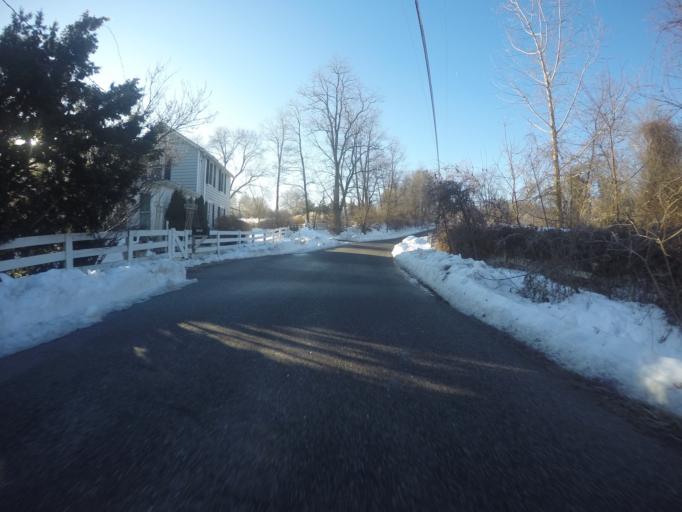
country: US
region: Maryland
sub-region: Baltimore County
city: Hunt Valley
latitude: 39.5389
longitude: -76.6688
